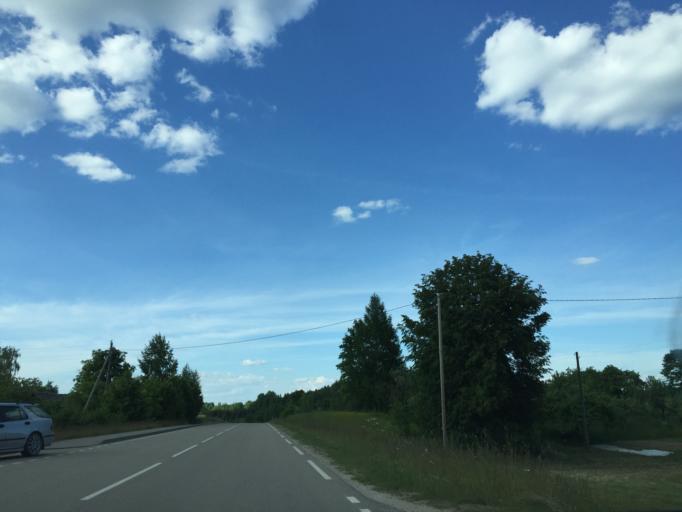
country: LV
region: Preilu Rajons
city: Jaunaglona
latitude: 56.2433
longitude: 27.2154
